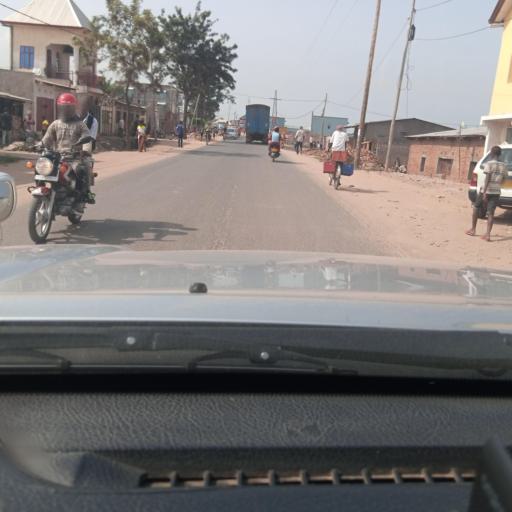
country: BI
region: Bujumbura Mairie
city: Bujumbura
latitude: -3.4356
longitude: 29.3541
